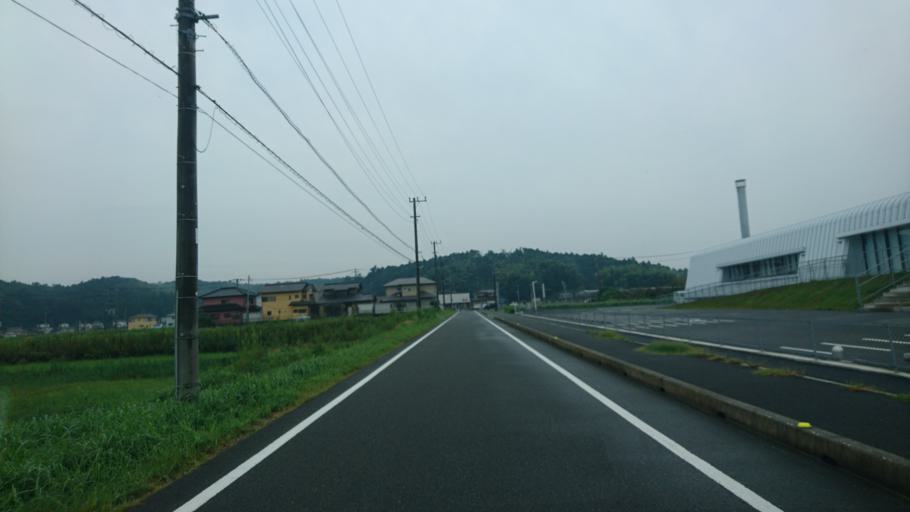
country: JP
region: Chiba
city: Kimitsu
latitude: 35.3065
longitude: 139.9628
